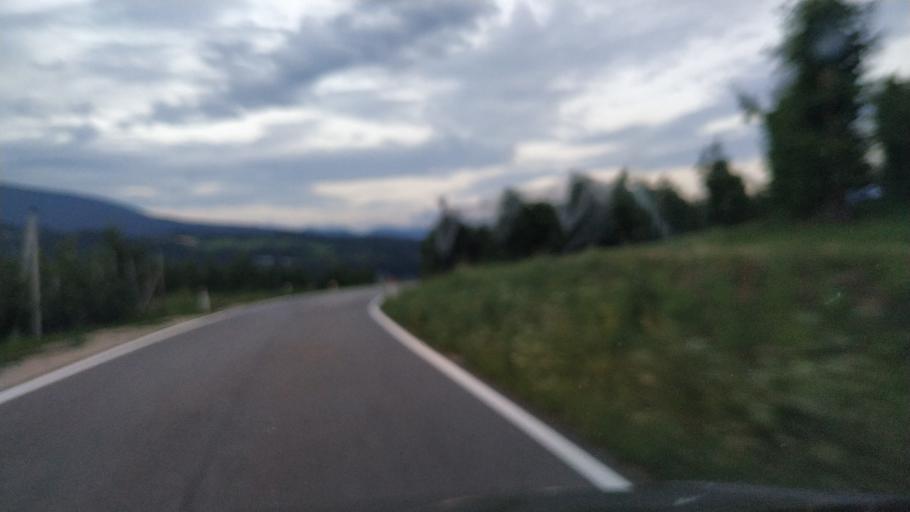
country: IT
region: Trentino-Alto Adige
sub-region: Provincia di Trento
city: Brez
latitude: 46.4398
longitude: 11.1114
